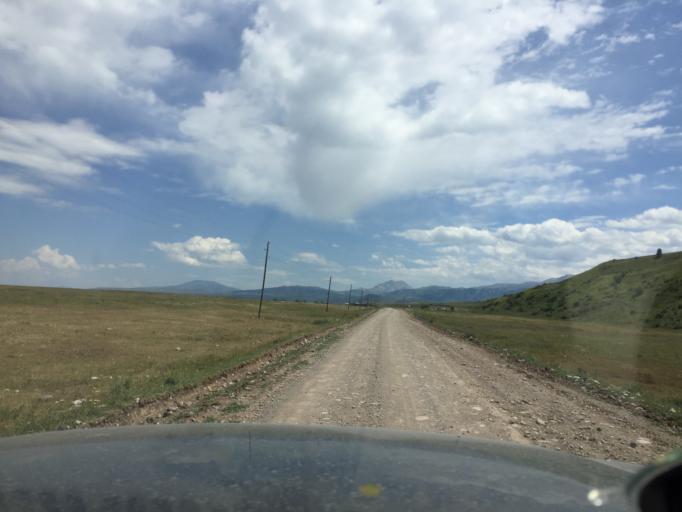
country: KZ
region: Almaty Oblysy
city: Kegen
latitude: 42.7580
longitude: 79.1592
